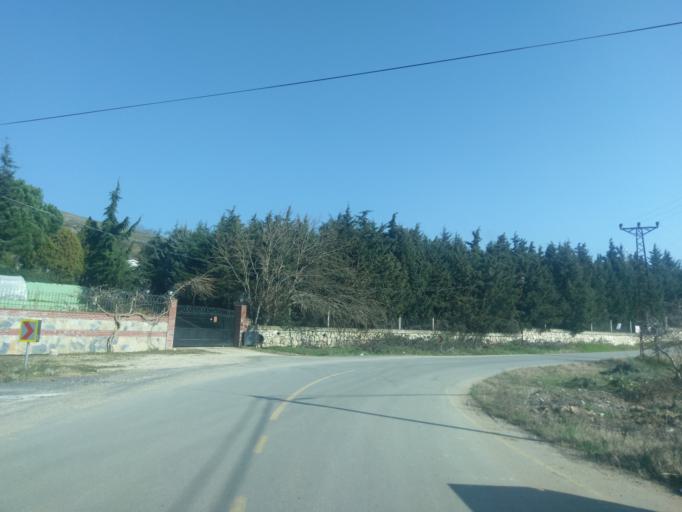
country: TR
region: Istanbul
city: Catalca
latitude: 41.1281
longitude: 28.4423
